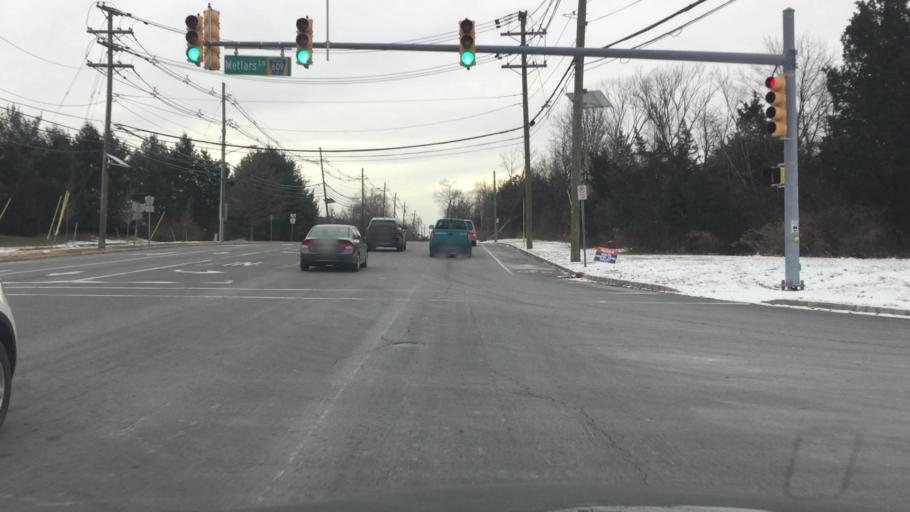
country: US
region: New Jersey
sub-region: Middlesex County
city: Society Hill
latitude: 40.5319
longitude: -74.4427
